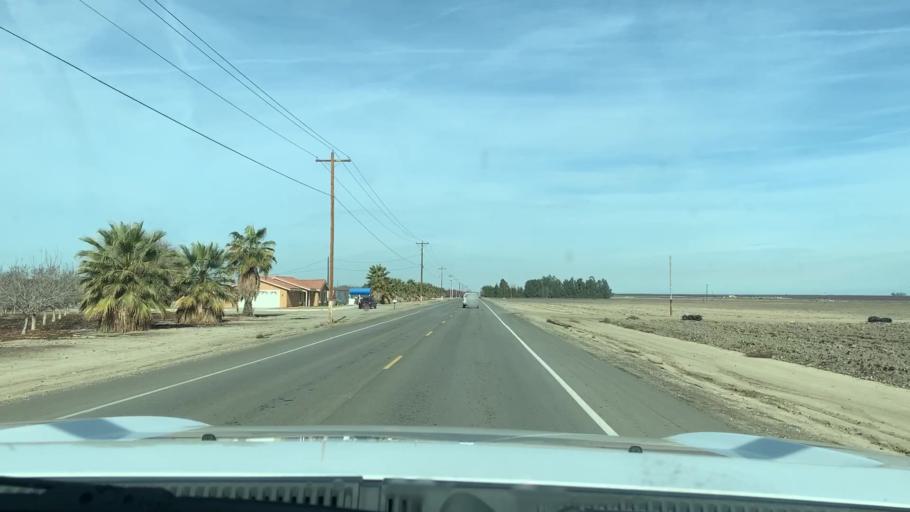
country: US
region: California
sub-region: Kern County
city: Buttonwillow
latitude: 35.5034
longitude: -119.4747
